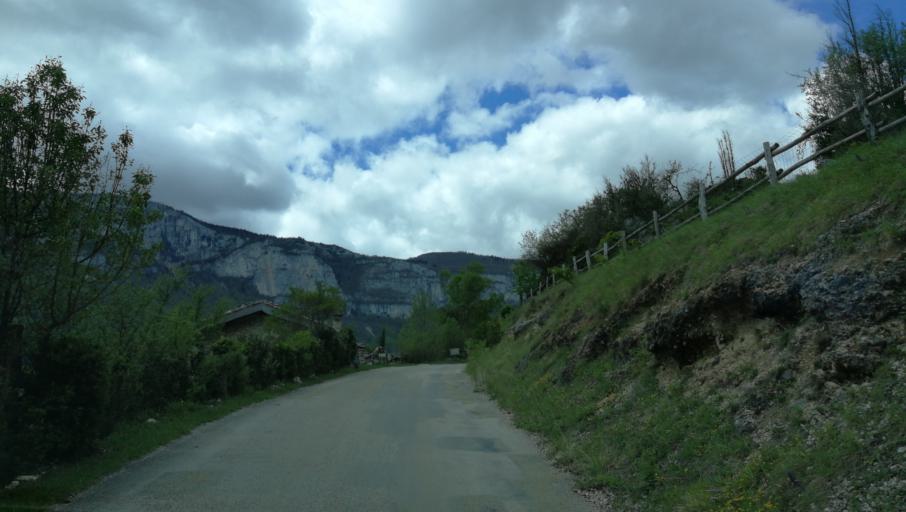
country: FR
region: Rhone-Alpes
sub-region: Departement de l'Isere
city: Pont-en-Royans
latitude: 45.0639
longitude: 5.4197
